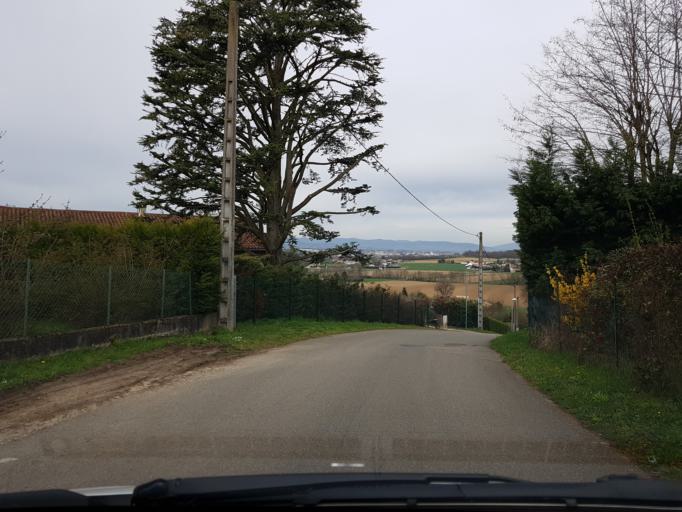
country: FR
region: Rhone-Alpes
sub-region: Departement de l'Ain
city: Trevoux
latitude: 45.9488
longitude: 4.7646
